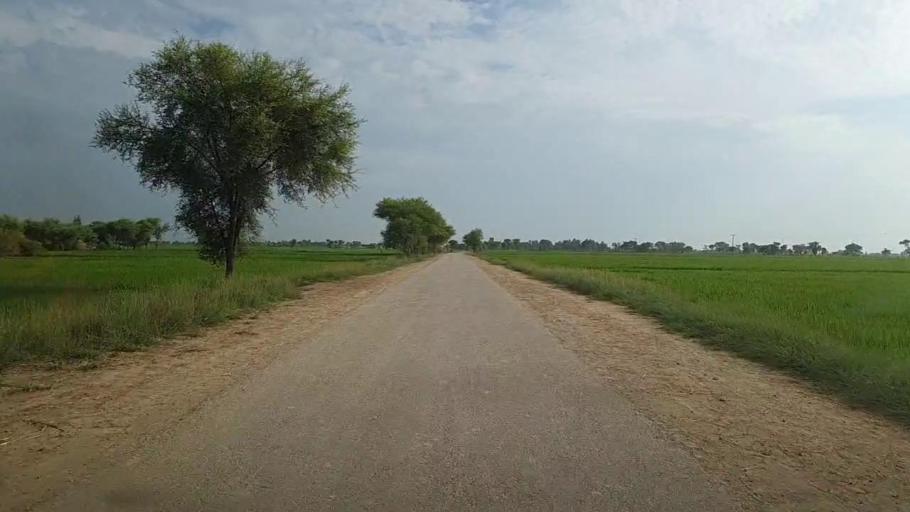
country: PK
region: Sindh
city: Thul
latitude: 28.2635
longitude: 68.8595
